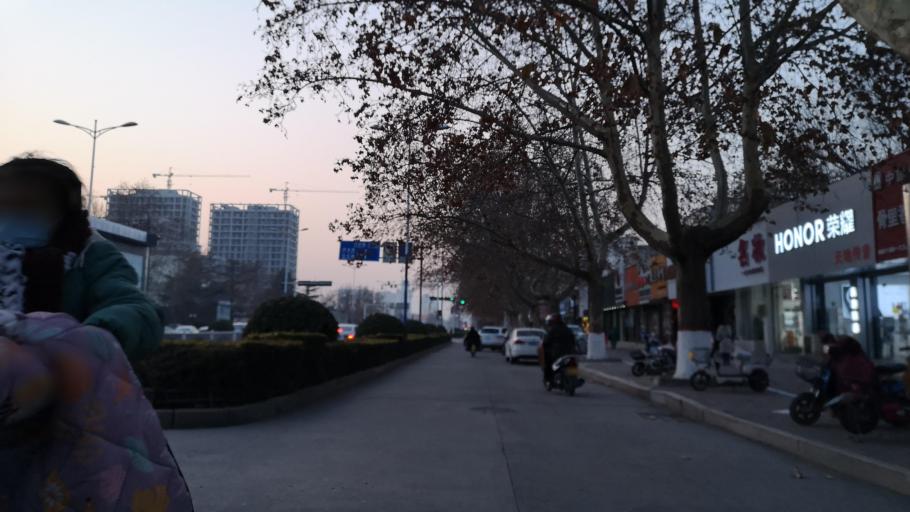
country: CN
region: Henan Sheng
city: Zhongyuanlu
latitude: 35.7758
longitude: 115.0773
